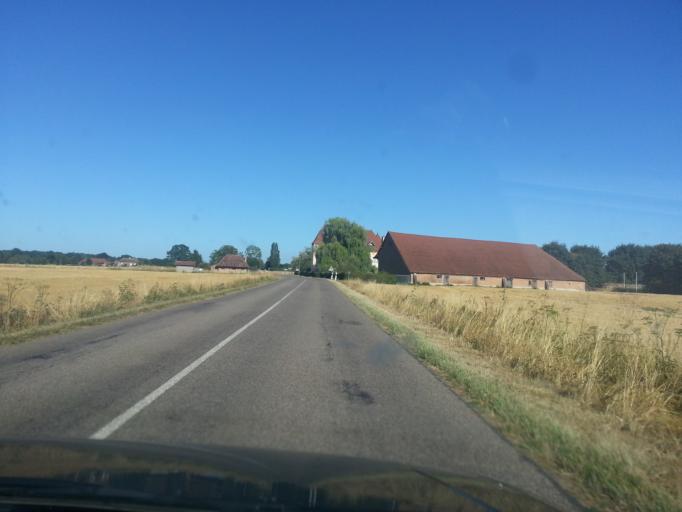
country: FR
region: Bourgogne
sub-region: Departement de Saone-et-Loire
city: Saint-Martin-en-Bresse
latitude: 46.8133
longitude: 5.0806
